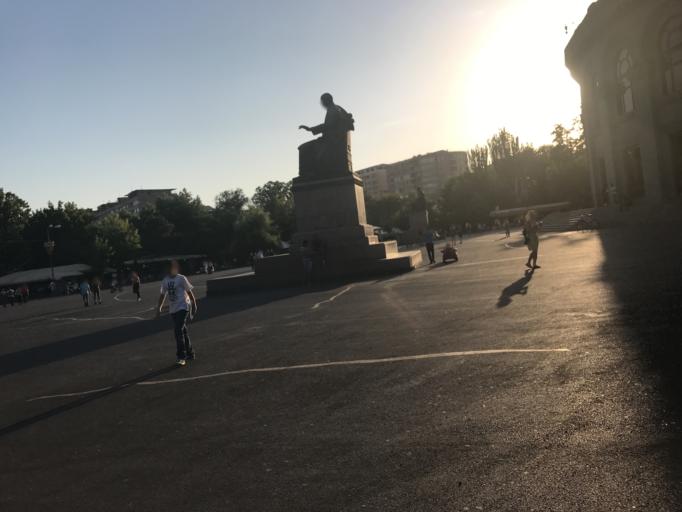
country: AM
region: Yerevan
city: Yerevan
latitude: 40.1855
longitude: 44.5157
